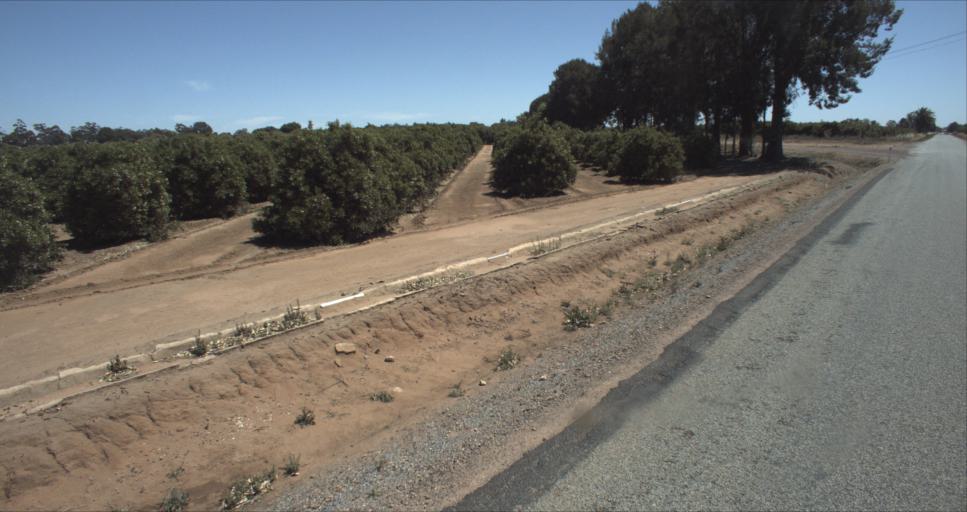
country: AU
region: New South Wales
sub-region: Leeton
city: Leeton
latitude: -34.5474
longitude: 146.3700
